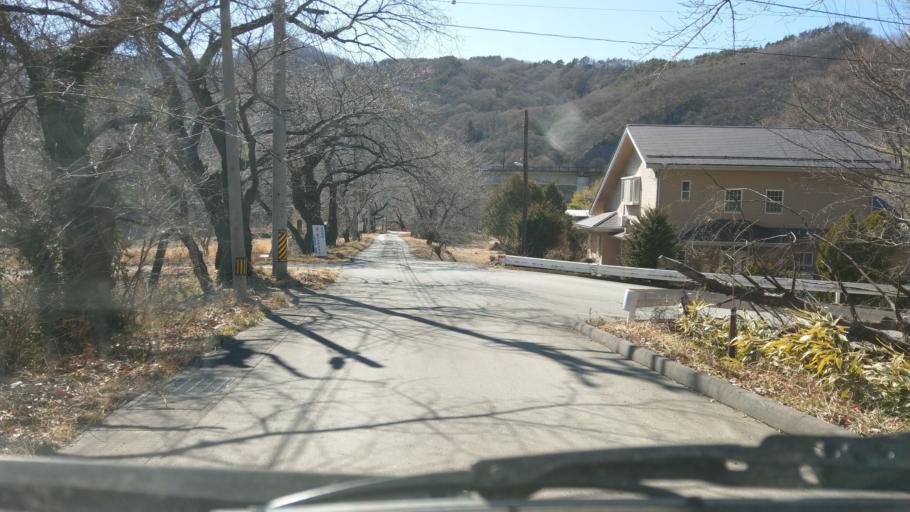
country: JP
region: Nagano
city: Komoro
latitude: 36.3328
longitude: 138.3948
